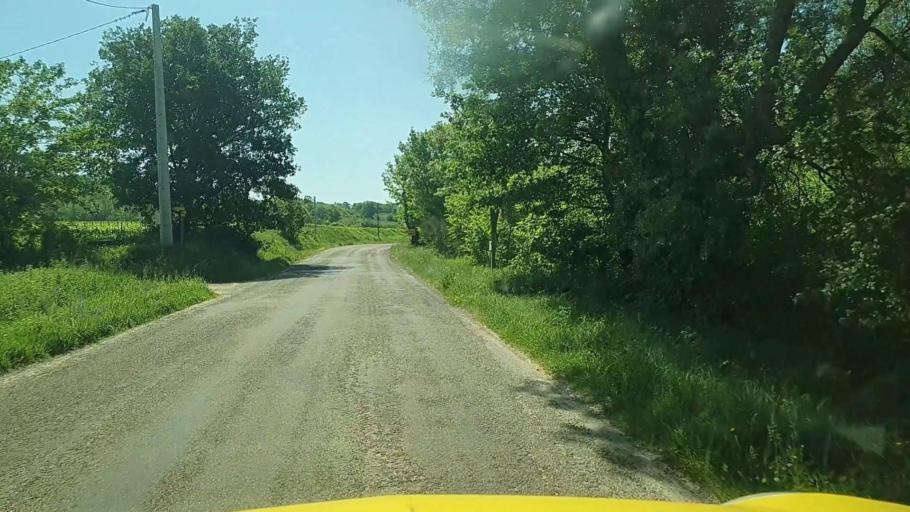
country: FR
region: Languedoc-Roussillon
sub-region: Departement du Gard
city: Moussac
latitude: 43.9904
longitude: 4.2217
